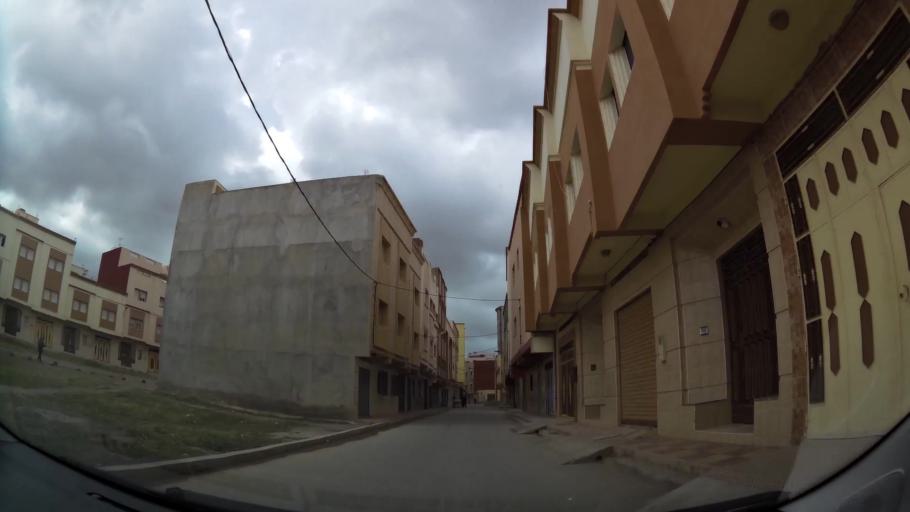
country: MA
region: Oriental
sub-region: Nador
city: Nador
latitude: 35.1665
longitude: -2.9390
